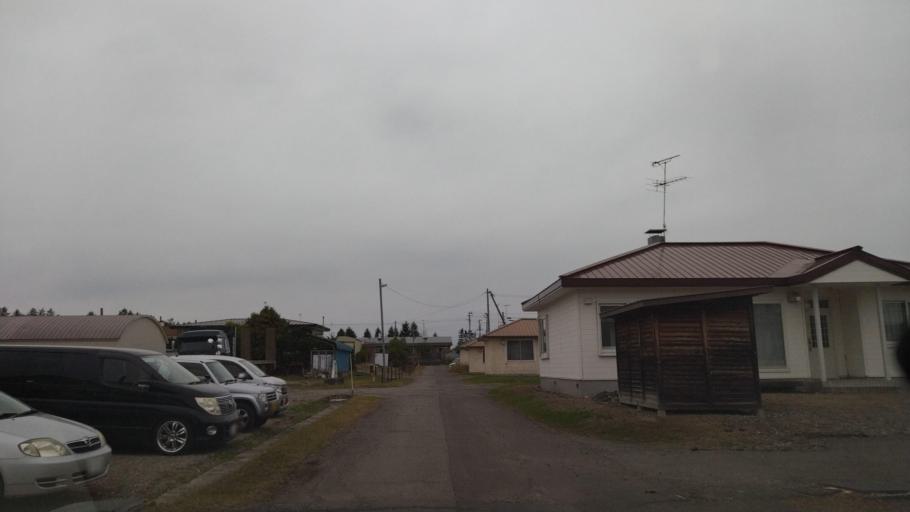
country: JP
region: Hokkaido
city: Otofuke
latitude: 43.2322
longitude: 143.2793
